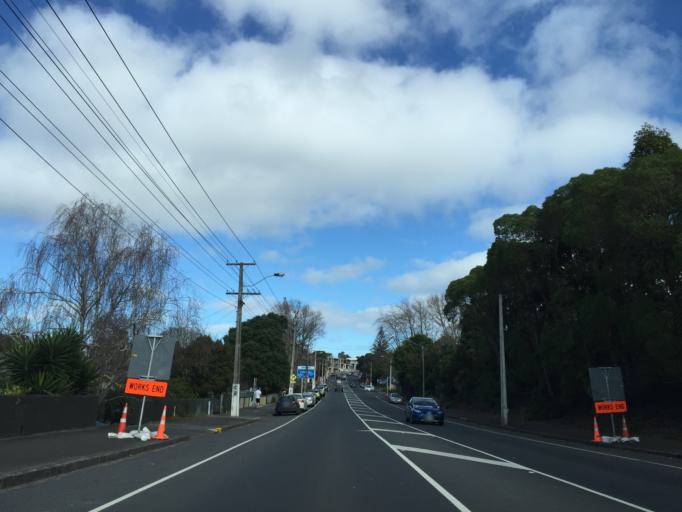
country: NZ
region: Auckland
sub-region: Auckland
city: Auckland
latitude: -36.9060
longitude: 174.7591
